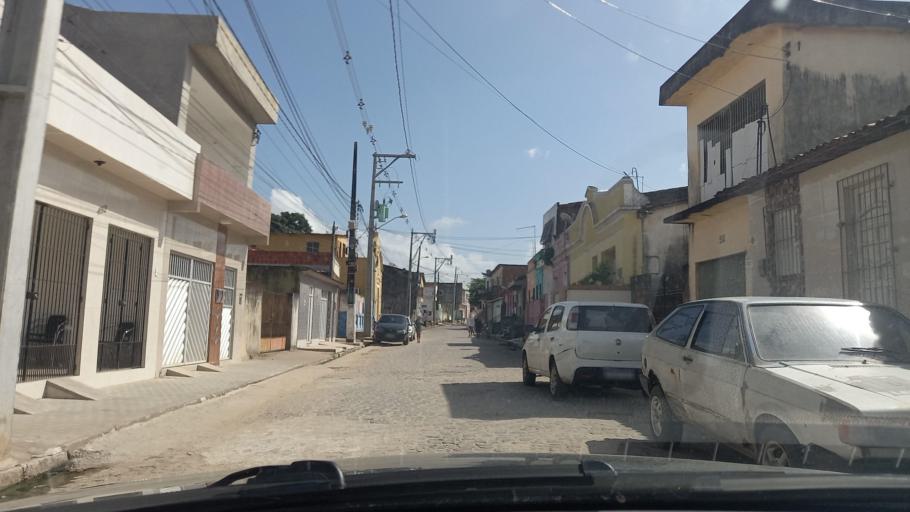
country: BR
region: Pernambuco
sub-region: Goiana
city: Goiana
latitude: -7.5660
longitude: -35.0099
